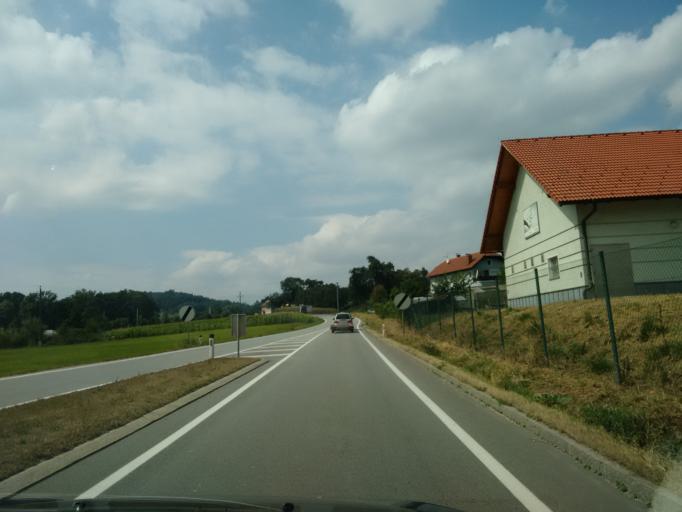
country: AT
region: Upper Austria
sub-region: Politischer Bezirk Grieskirchen
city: Bad Schallerbach
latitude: 48.2212
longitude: 13.9452
